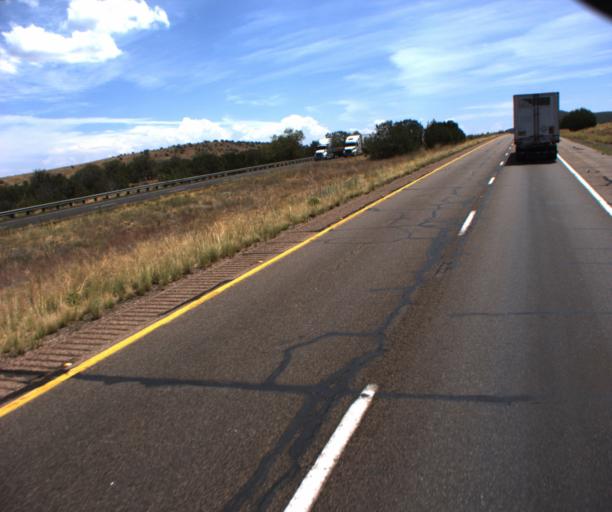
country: US
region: Arizona
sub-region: Yavapai County
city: Paulden
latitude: 35.2791
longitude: -112.7807
